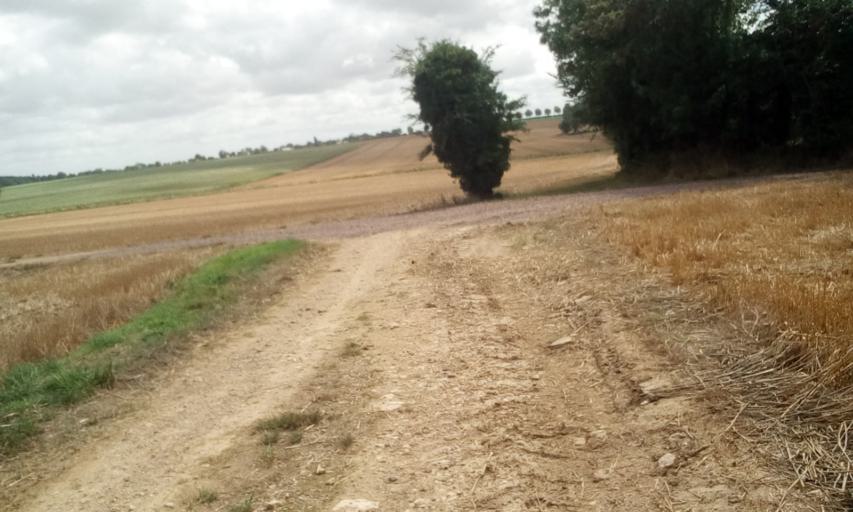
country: FR
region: Lower Normandy
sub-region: Departement du Calvados
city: Cheux
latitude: 49.1861
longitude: -0.5309
